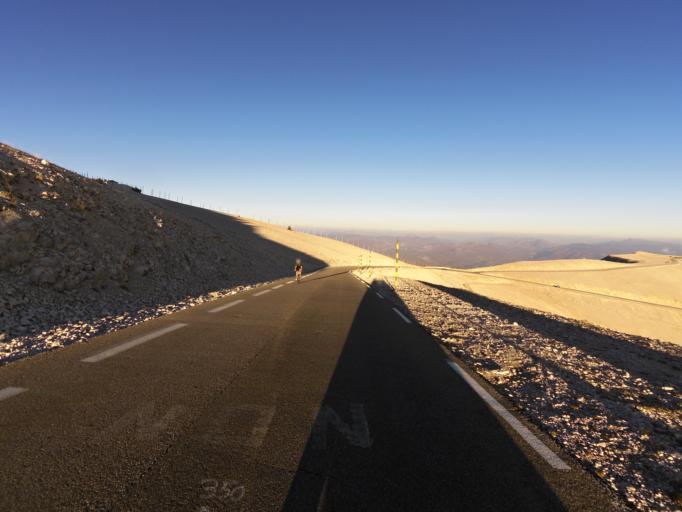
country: FR
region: Rhone-Alpes
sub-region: Departement de la Drome
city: Buis-les-Baronnies
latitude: 44.1733
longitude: 5.2798
